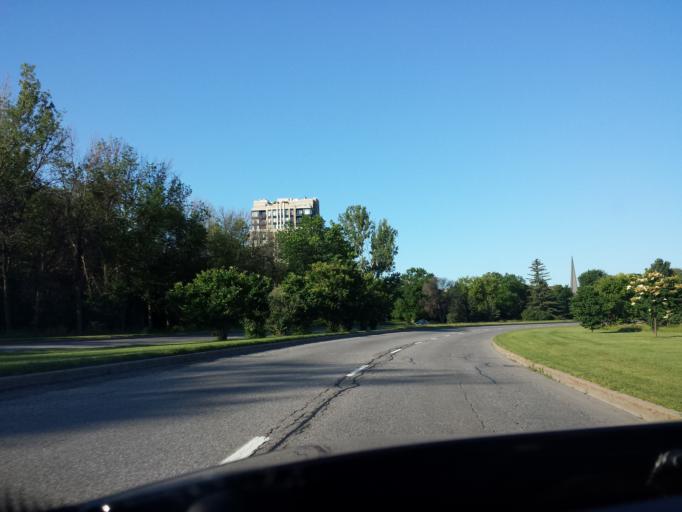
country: CA
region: Ontario
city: Ottawa
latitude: 45.3845
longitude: -75.7692
